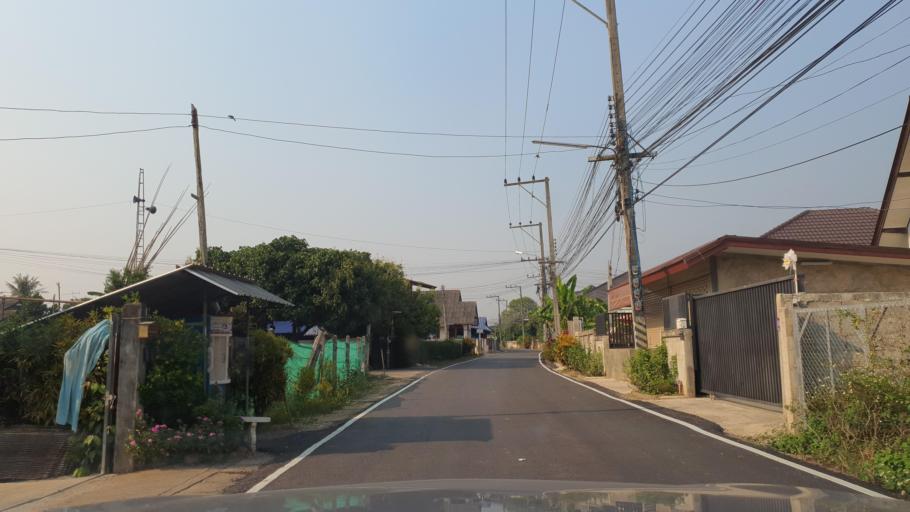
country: TH
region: Chiang Mai
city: Mae Taeng
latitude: 19.1354
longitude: 99.0095
